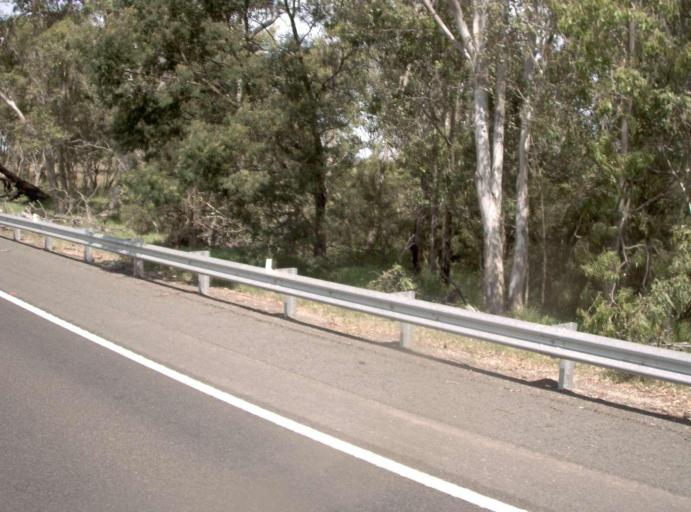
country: AU
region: Victoria
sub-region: East Gippsland
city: Bairnsdale
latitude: -37.8764
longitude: 147.4434
